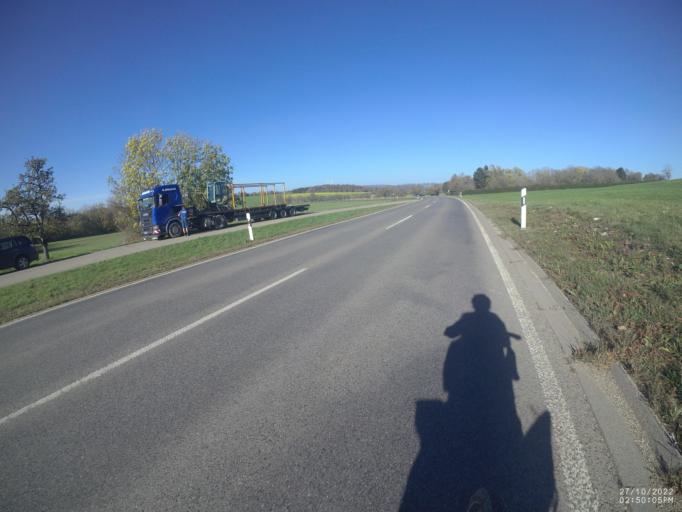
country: DE
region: Baden-Wuerttemberg
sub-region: Regierungsbezirk Stuttgart
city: Bad Uberkingen
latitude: 48.5947
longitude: 9.8151
